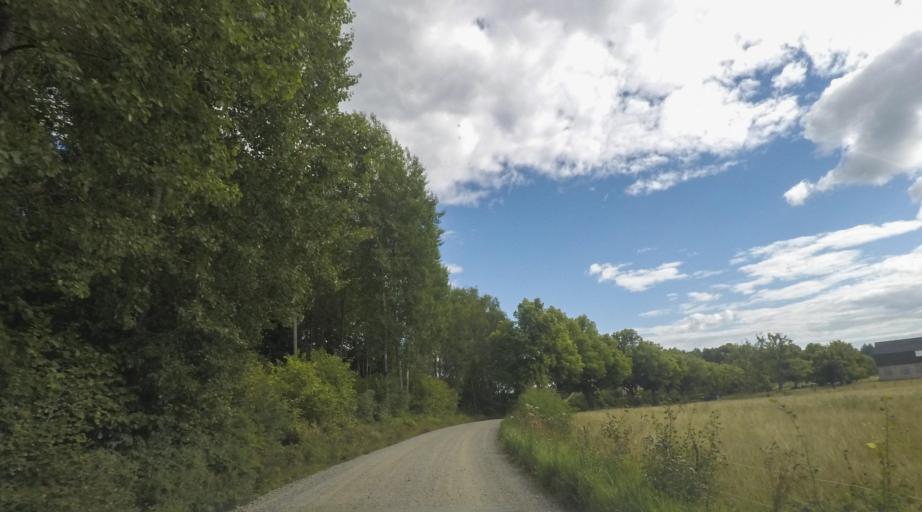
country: SE
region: Stockholm
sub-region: Sodertalje Kommun
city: Pershagen
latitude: 59.1151
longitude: 17.6587
